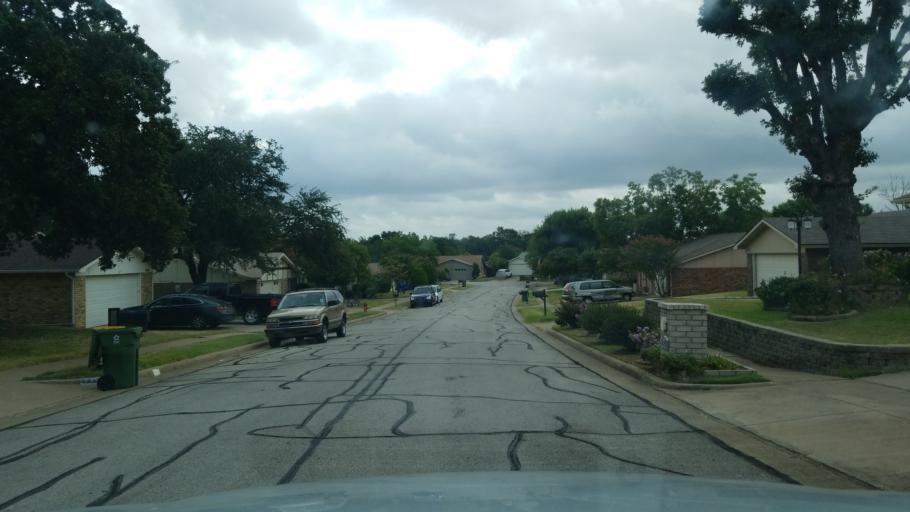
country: US
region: Texas
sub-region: Tarrant County
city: Euless
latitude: 32.8460
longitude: -97.1059
